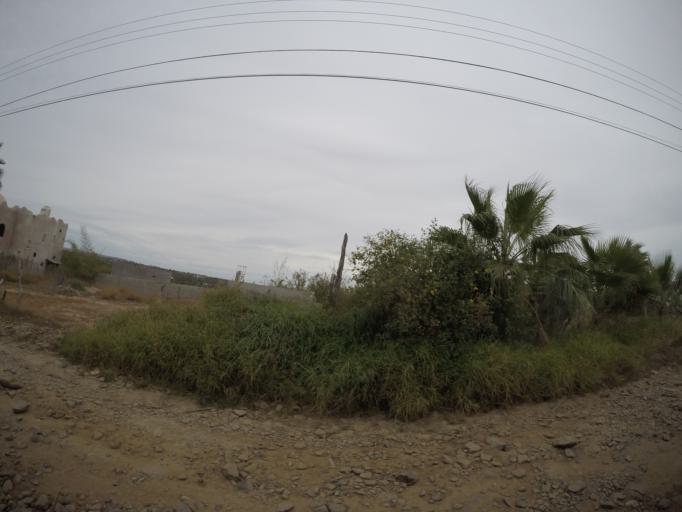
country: MX
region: Baja California Sur
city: Todos Santos
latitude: 23.4406
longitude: -110.2343
